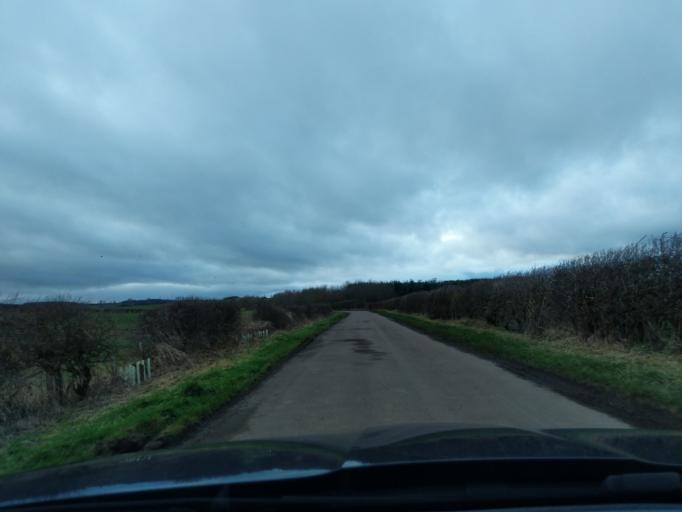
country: GB
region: England
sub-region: Northumberland
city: Ancroft
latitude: 55.7023
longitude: -2.0195
